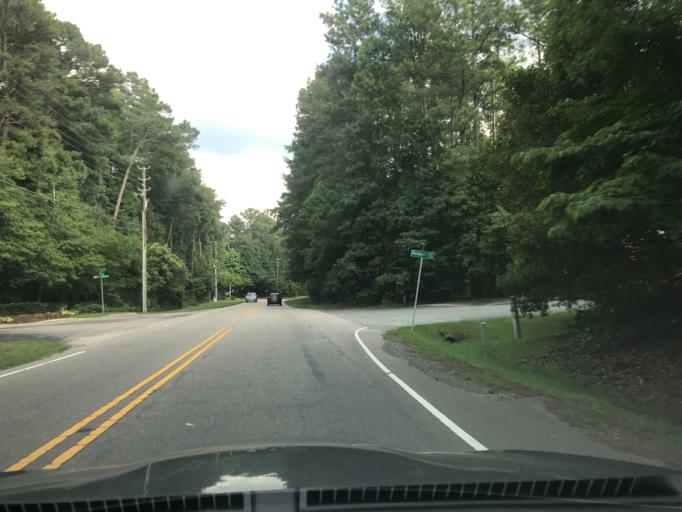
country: US
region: North Carolina
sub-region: Wake County
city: West Raleigh
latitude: 35.8765
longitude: -78.7031
